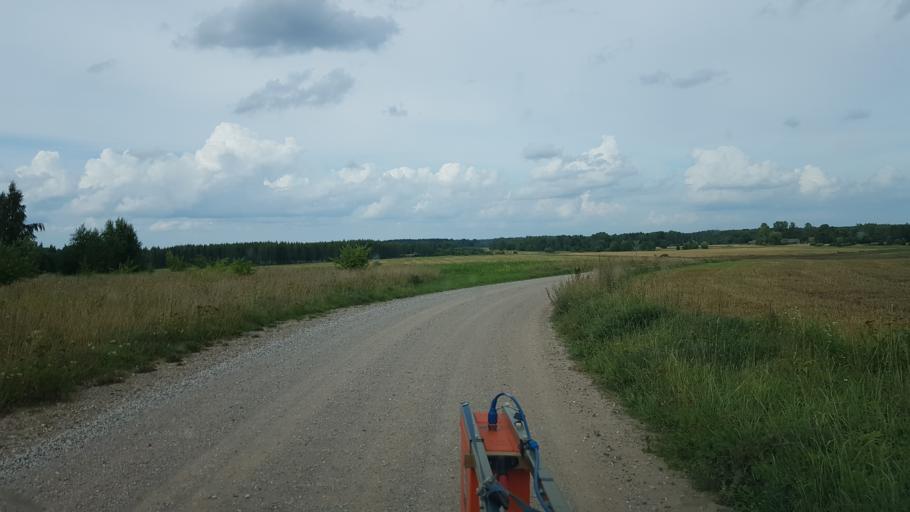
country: RU
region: Pskov
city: Pechory
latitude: 57.7988
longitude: 27.5016
